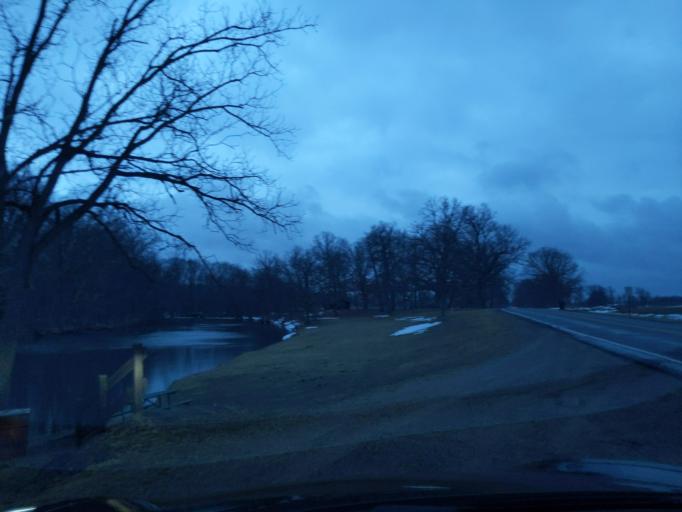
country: US
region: Michigan
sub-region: Eaton County
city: Eaton Rapids
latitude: 42.4395
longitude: -84.5604
